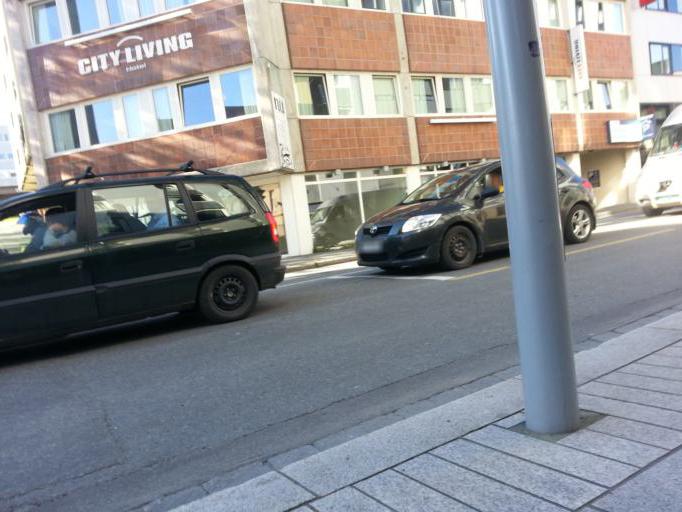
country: NO
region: Troms
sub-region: Tromso
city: Tromso
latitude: 69.6481
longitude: 18.9529
